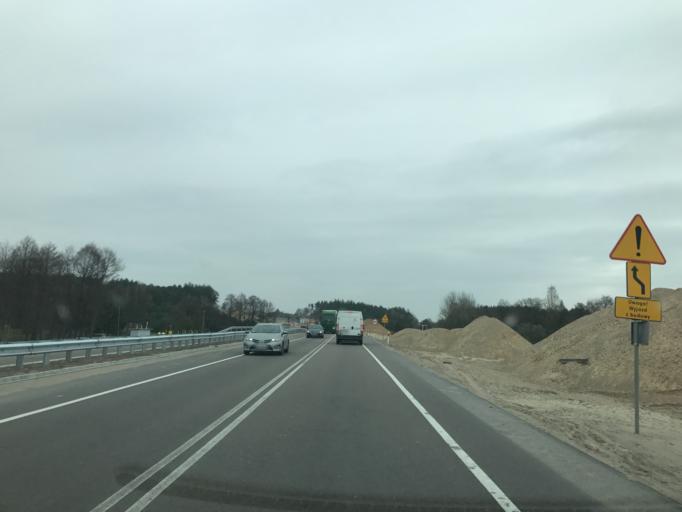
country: PL
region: Warmian-Masurian Voivodeship
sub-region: Powiat olsztynski
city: Olsztynek
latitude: 53.6108
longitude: 20.3257
